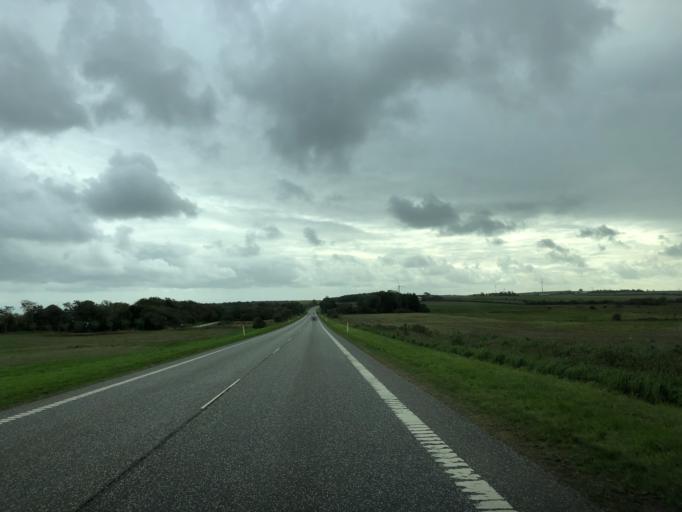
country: DK
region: North Denmark
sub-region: Thisted Kommune
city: Hurup
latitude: 56.7871
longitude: 8.4679
